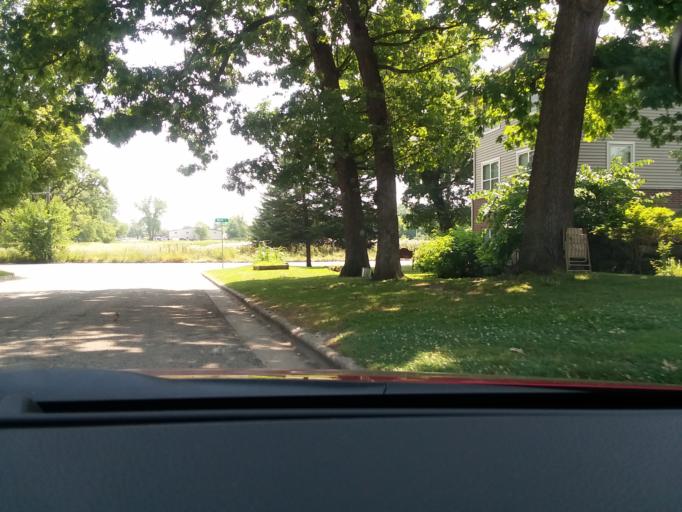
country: US
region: Wisconsin
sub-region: Dane County
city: Maple Bluff
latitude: 43.1118
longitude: -89.3615
